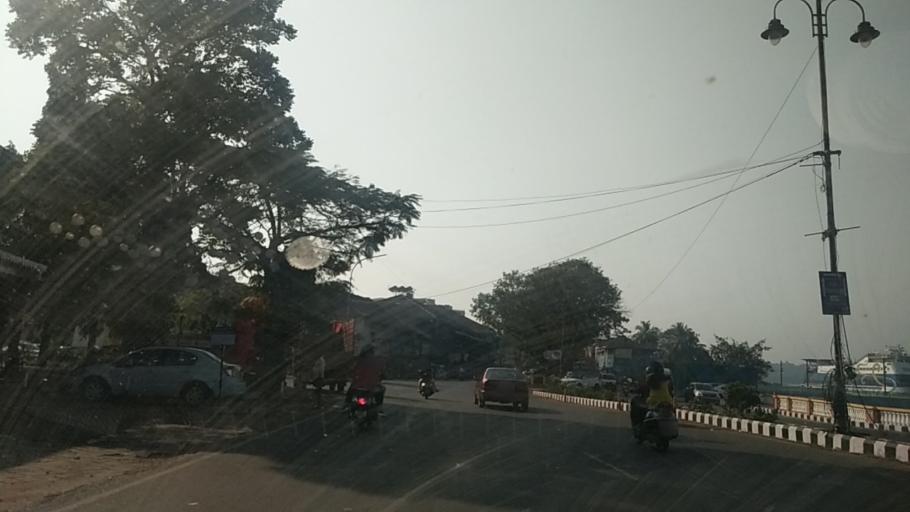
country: IN
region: Goa
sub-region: North Goa
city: Panaji
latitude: 15.5010
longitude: 73.8299
